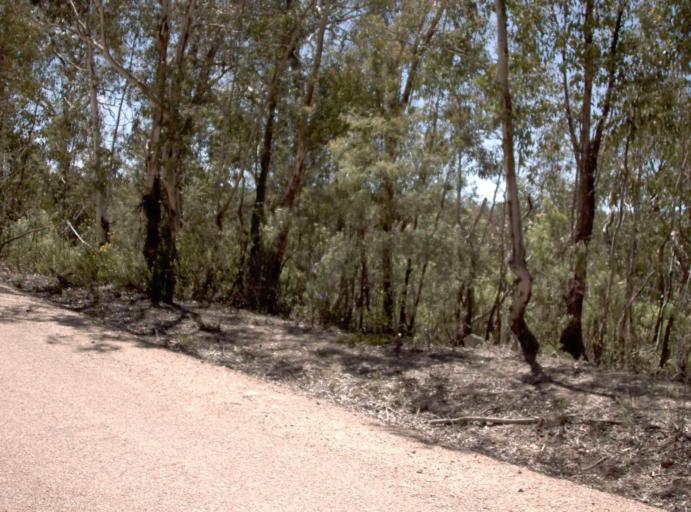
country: AU
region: New South Wales
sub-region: Snowy River
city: Jindabyne
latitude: -37.0479
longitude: 148.2765
